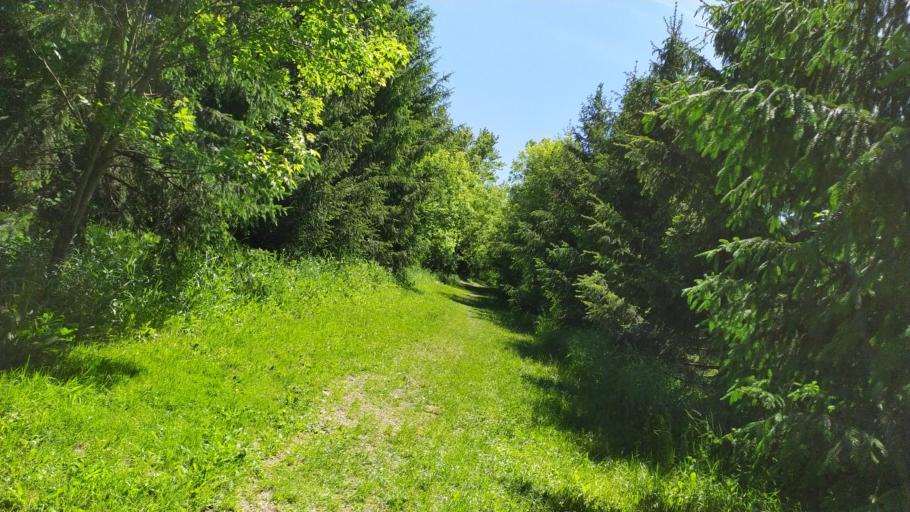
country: CA
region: Ontario
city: Stratford
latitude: 43.3684
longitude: -81.0043
